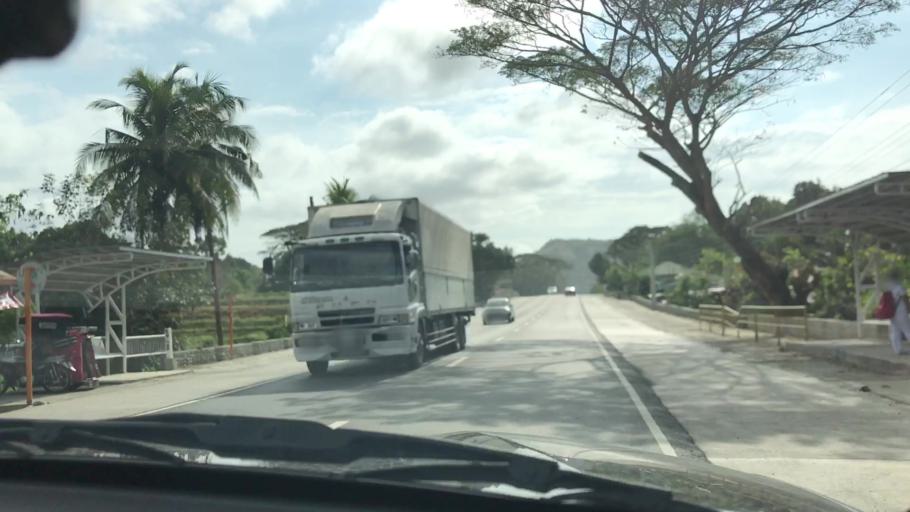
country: PH
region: Ilocos
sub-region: Province of La Union
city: Butubut Norte
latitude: 16.7759
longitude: 120.4127
